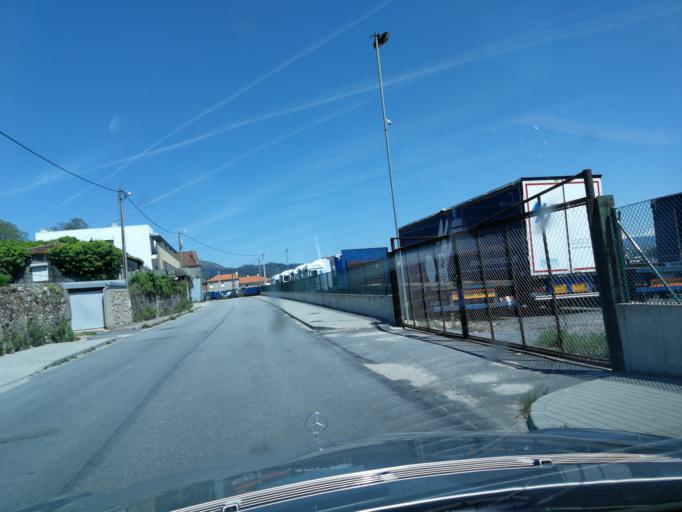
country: PT
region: Viana do Castelo
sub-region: Viana do Castelo
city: Meadela
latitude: 41.7124
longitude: -8.8022
